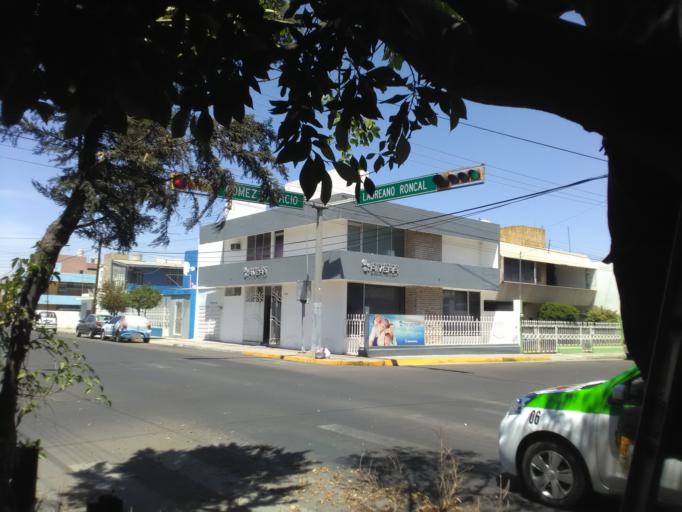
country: MX
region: Durango
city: Victoria de Durango
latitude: 24.0324
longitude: -104.6593
